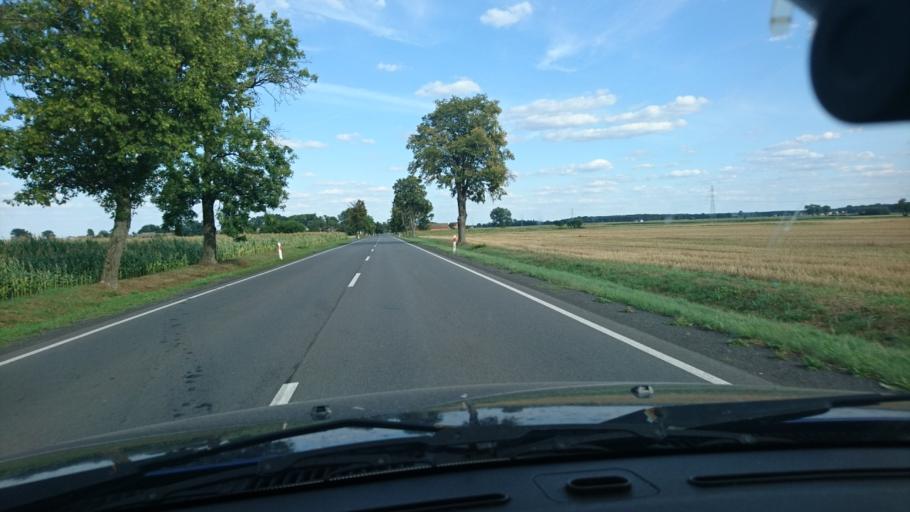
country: PL
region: Greater Poland Voivodeship
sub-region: Powiat krotoszynski
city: Zduny
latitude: 51.7202
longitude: 17.3573
